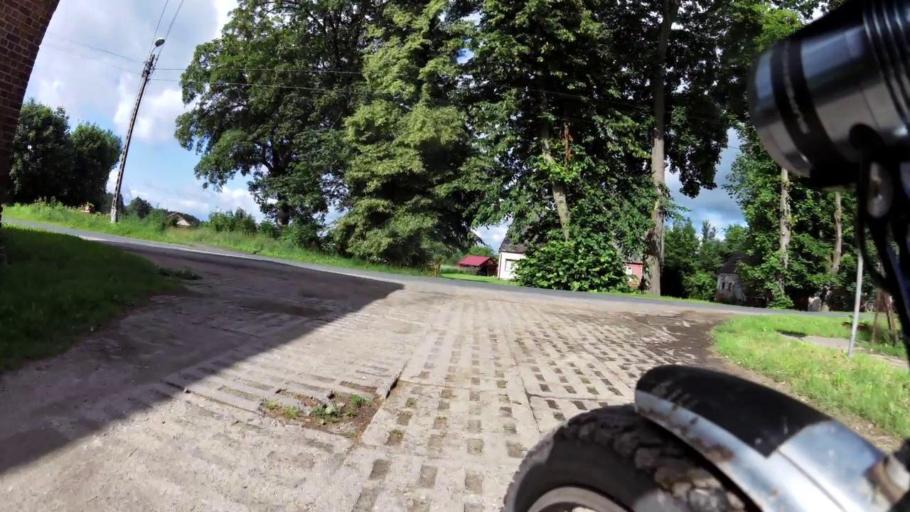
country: PL
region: West Pomeranian Voivodeship
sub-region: Powiat swidwinski
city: Rabino
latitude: 53.7568
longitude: 15.9121
